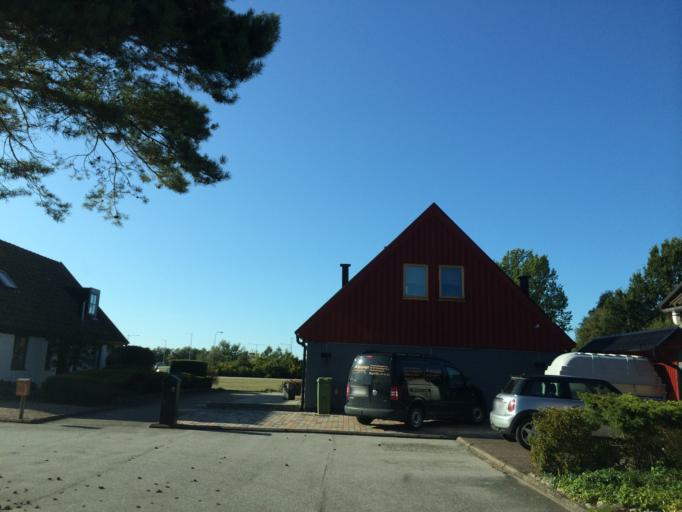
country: SE
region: Skane
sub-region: Kavlinge Kommun
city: Loddekopinge
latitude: 55.7648
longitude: 12.9923
